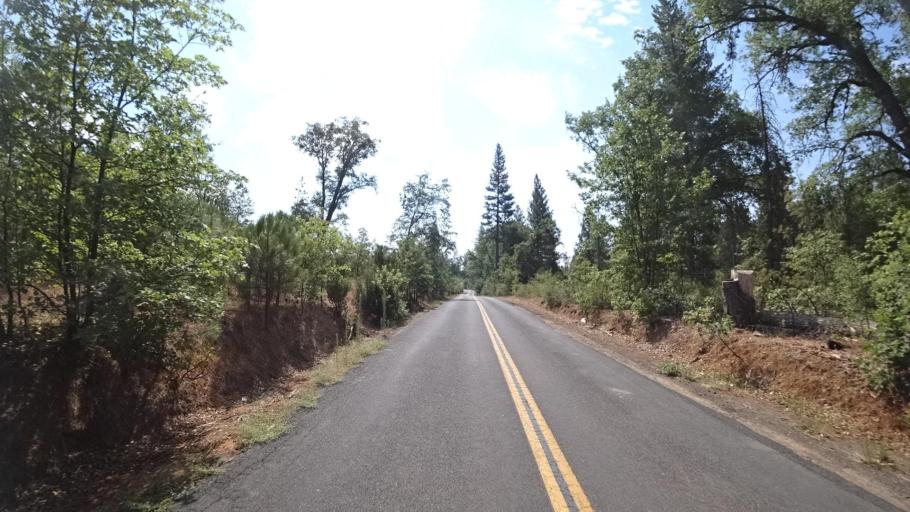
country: US
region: California
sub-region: Tuolumne County
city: Tuolumne City
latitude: 37.7674
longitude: -120.1544
